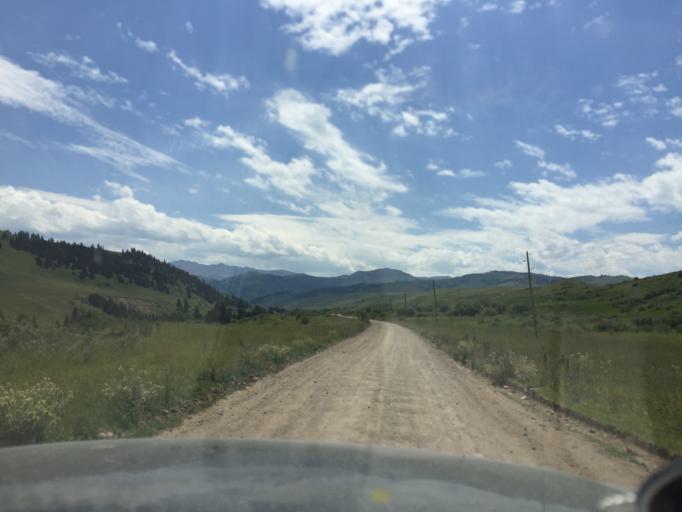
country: KZ
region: Almaty Oblysy
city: Kegen
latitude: 42.7451
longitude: 79.1688
